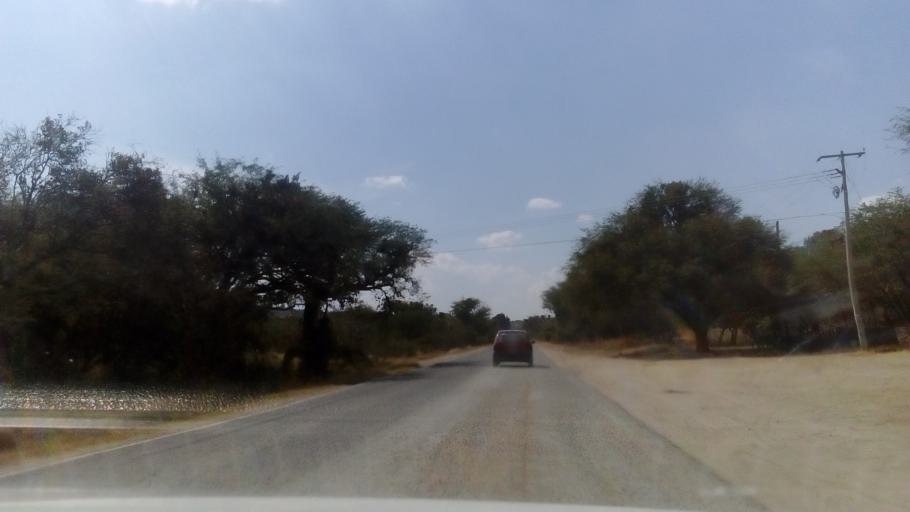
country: MX
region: Guanajuato
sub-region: Silao de la Victoria
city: San Francisco (Banos de Agua Caliente)
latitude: 21.0776
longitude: -101.4735
